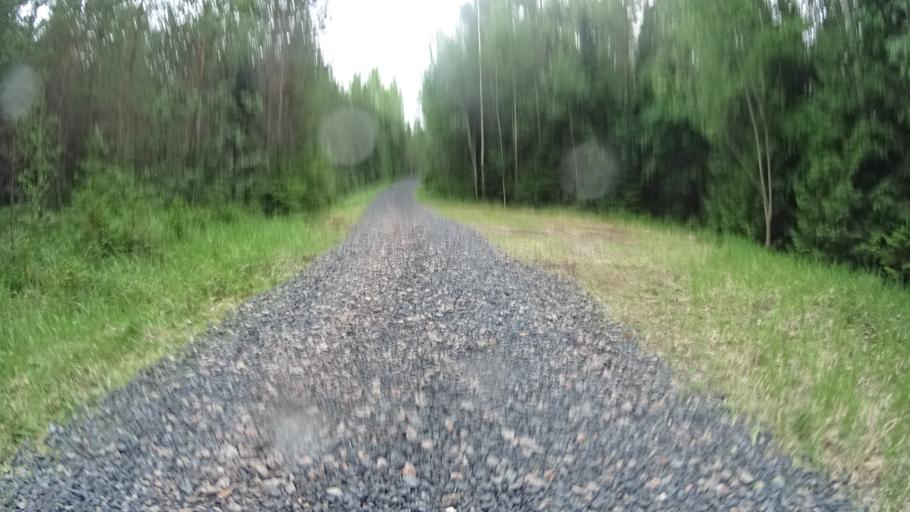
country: FI
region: Uusimaa
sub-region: Helsinki
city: Karkkila
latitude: 60.5861
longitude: 24.1551
